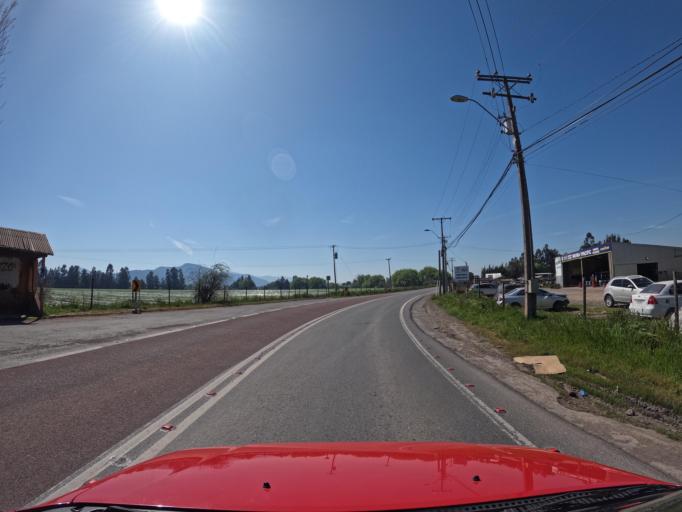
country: CL
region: Maule
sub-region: Provincia de Curico
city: Rauco
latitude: -35.0040
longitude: -71.3999
